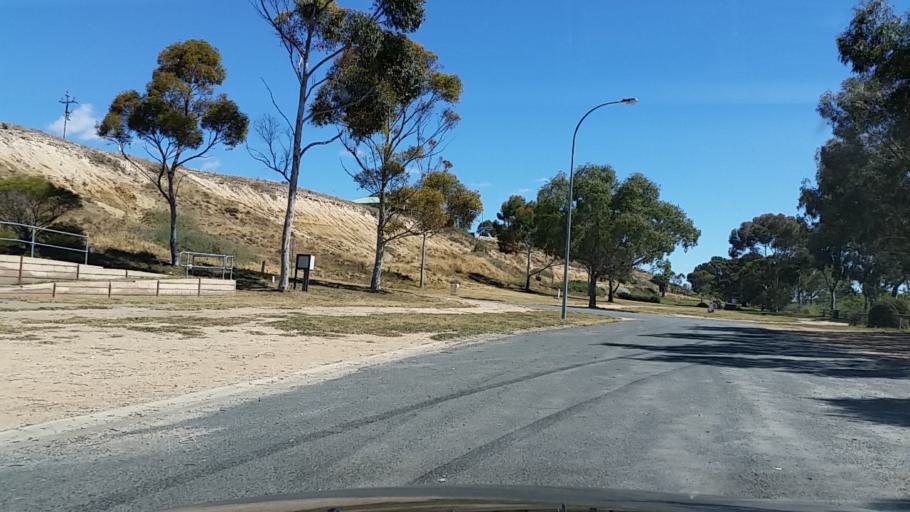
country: AU
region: South Australia
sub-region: Murray Bridge
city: Tailem Bend
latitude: -35.2866
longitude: 139.4482
